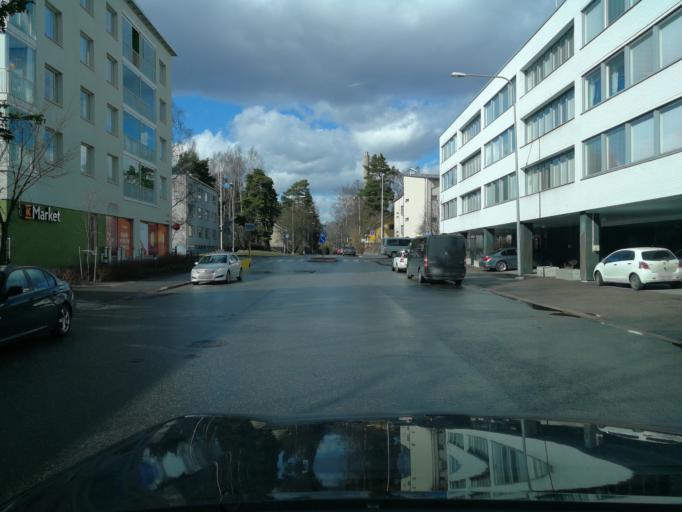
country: FI
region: Uusimaa
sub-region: Helsinki
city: Helsinki
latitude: 60.2019
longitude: 24.9056
